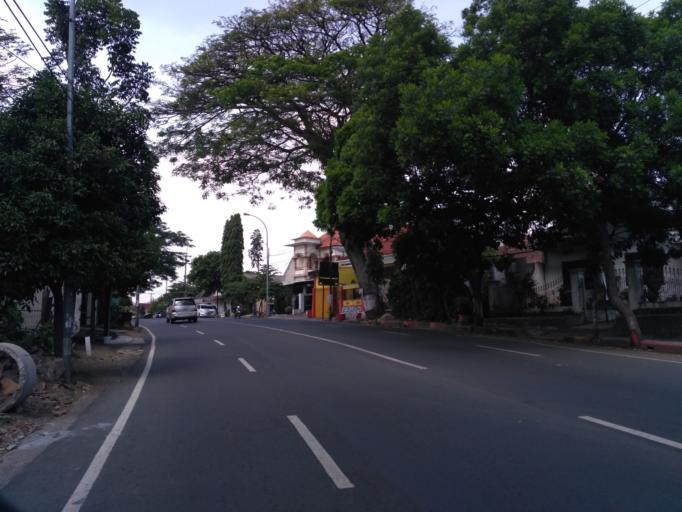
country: ID
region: East Java
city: Batu
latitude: -7.9090
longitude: 112.5792
